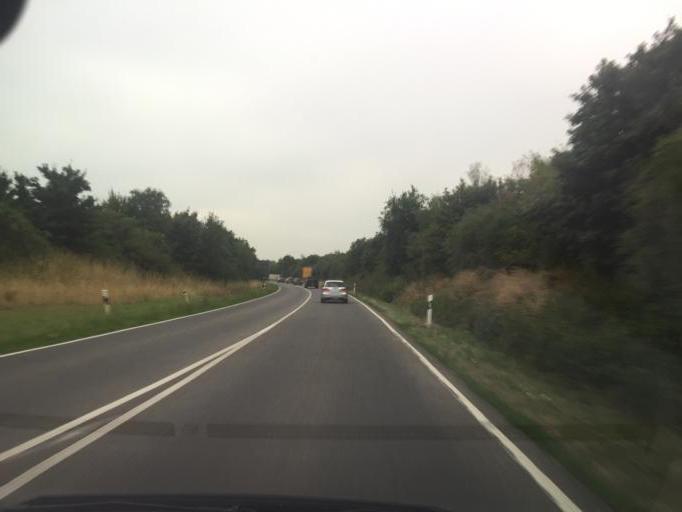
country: DE
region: North Rhine-Westphalia
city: Wegberg
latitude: 51.1563
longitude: 6.3520
